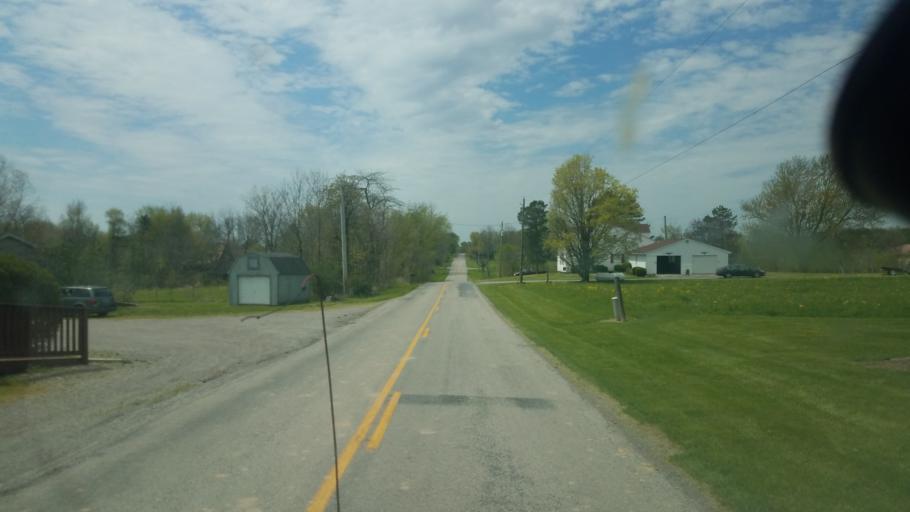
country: US
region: Ohio
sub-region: Allen County
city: Bluffton
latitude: 40.7853
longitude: -83.9620
